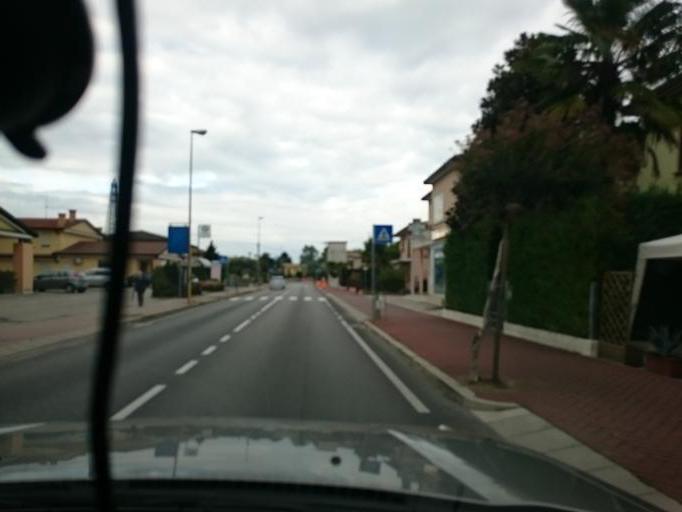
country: IT
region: Veneto
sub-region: Provincia di Padova
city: Saccolongo
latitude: 45.4075
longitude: 11.7391
